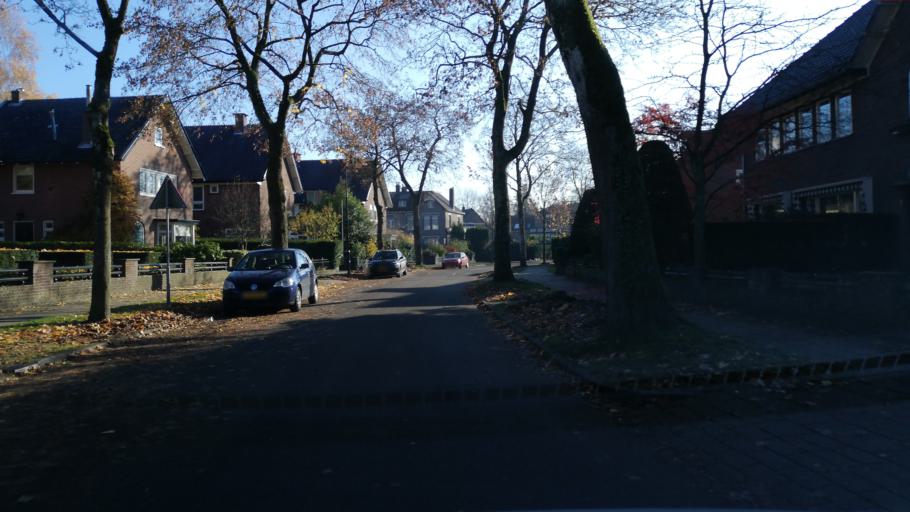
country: NL
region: Gelderland
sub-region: Gemeente Apeldoorn
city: Apeldoorn
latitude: 52.2194
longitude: 5.9652
